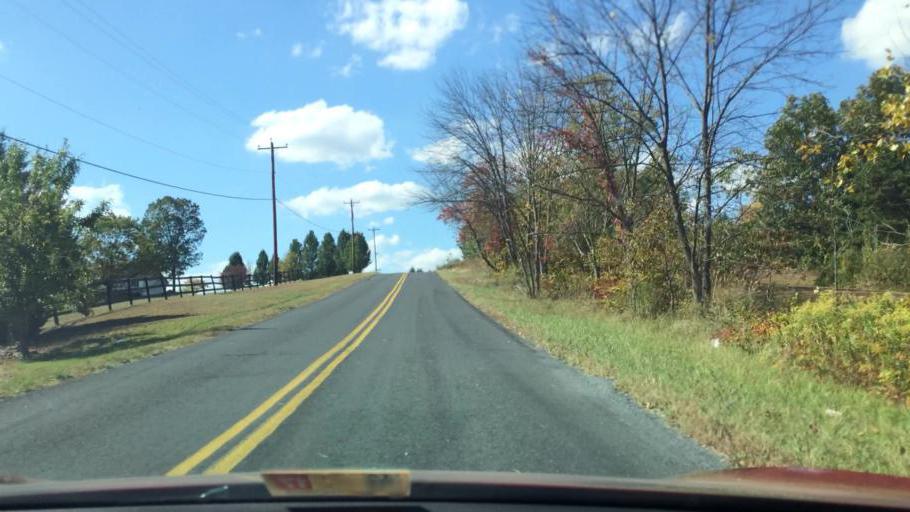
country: US
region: Virginia
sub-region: Frederick County
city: Shawnee Land
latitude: 39.3250
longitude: -78.3151
